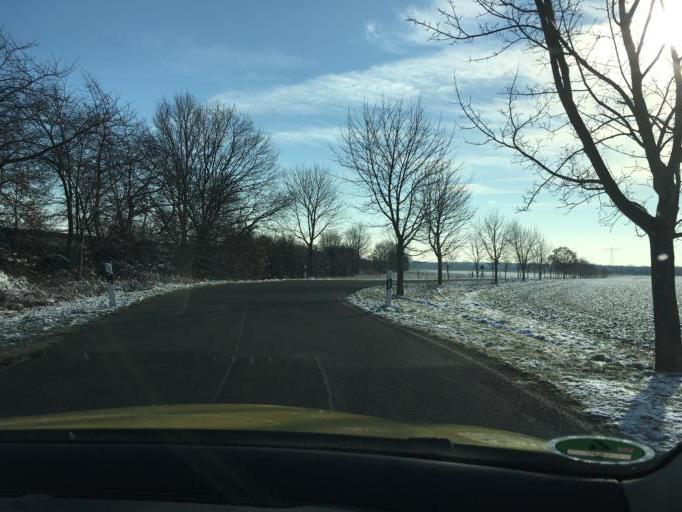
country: DE
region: Saxony
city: Belgershain
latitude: 51.2269
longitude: 12.5525
